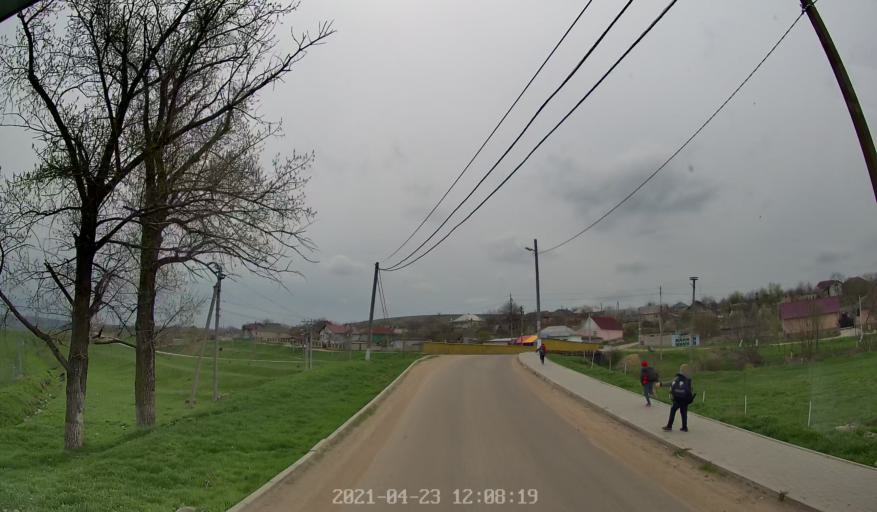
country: MD
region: Chisinau
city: Vadul lui Voda
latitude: 47.1206
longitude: 29.0019
